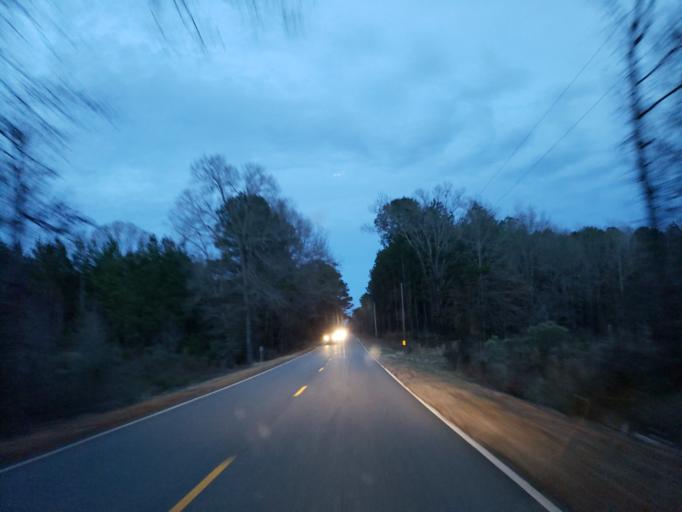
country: US
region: Alabama
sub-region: Greene County
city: Eutaw
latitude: 32.8832
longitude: -88.0618
